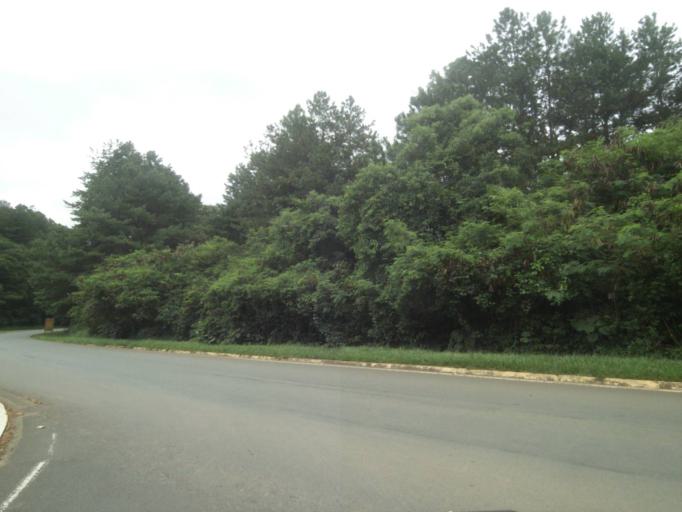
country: BR
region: Parana
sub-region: Telemaco Borba
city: Telemaco Borba
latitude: -24.3096
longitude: -50.6165
